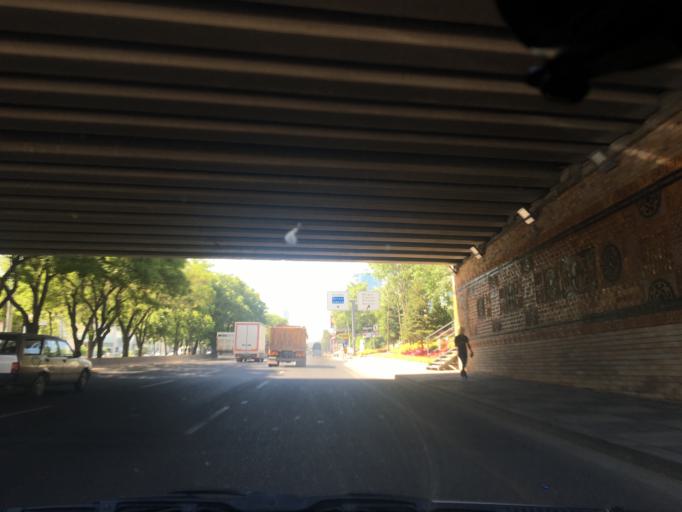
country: TR
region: Ankara
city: Ankara
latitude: 39.8973
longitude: 32.8133
